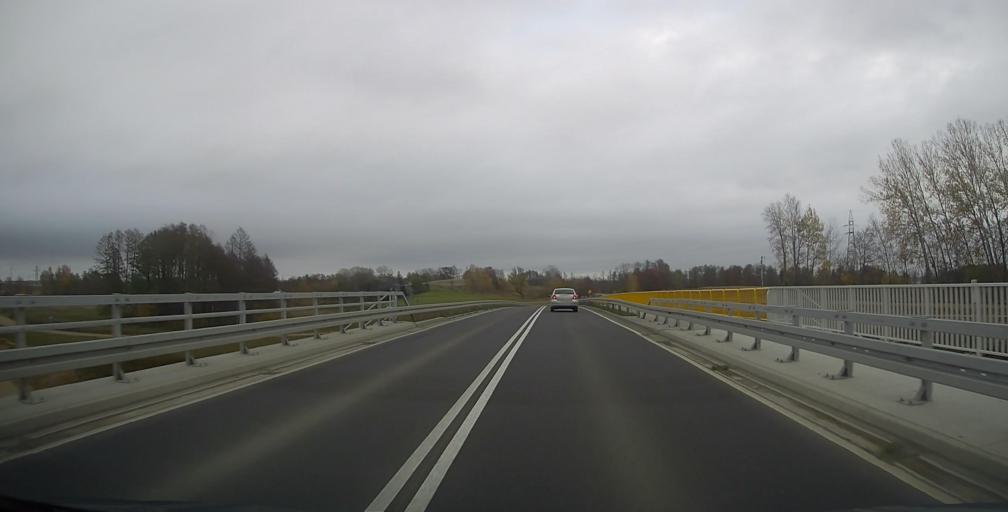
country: PL
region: Warmian-Masurian Voivodeship
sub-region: Powiat elcki
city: Elk
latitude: 53.8478
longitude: 22.4606
